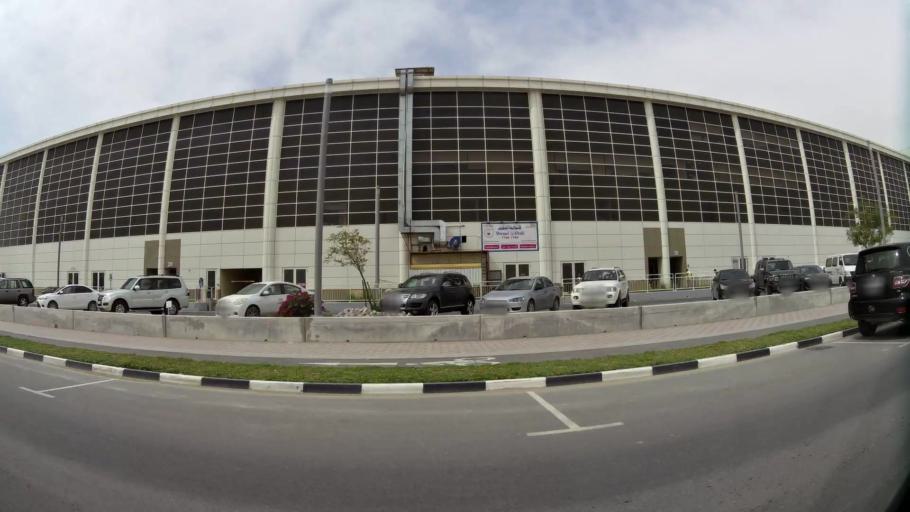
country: QA
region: Baladiyat ar Rayyan
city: Ar Rayyan
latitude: 25.1993
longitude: 51.4520
